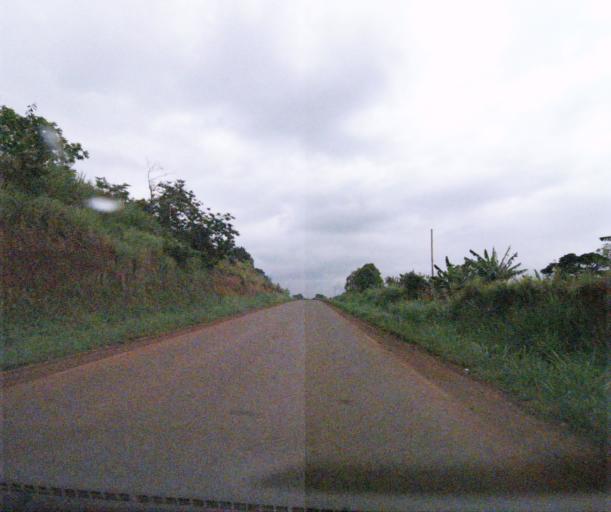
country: CM
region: West
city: Bansoa
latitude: 5.4941
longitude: 10.2240
